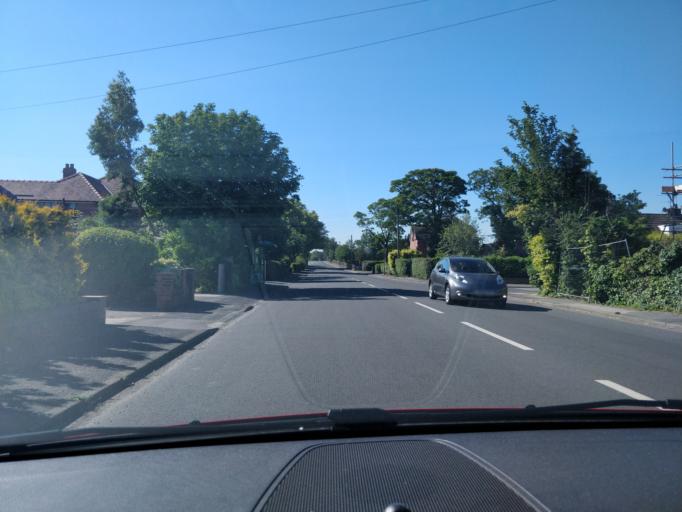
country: GB
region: England
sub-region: Lancashire
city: Tarleton
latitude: 53.7008
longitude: -2.8397
